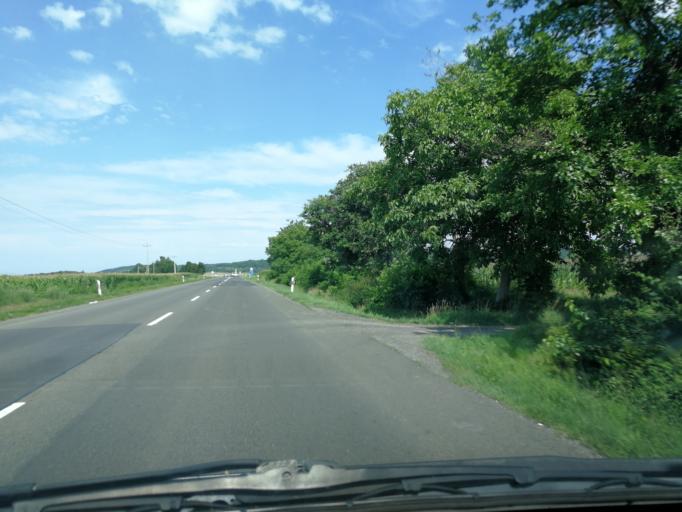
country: HU
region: Tolna
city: Bonyhad
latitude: 46.3185
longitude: 18.5622
